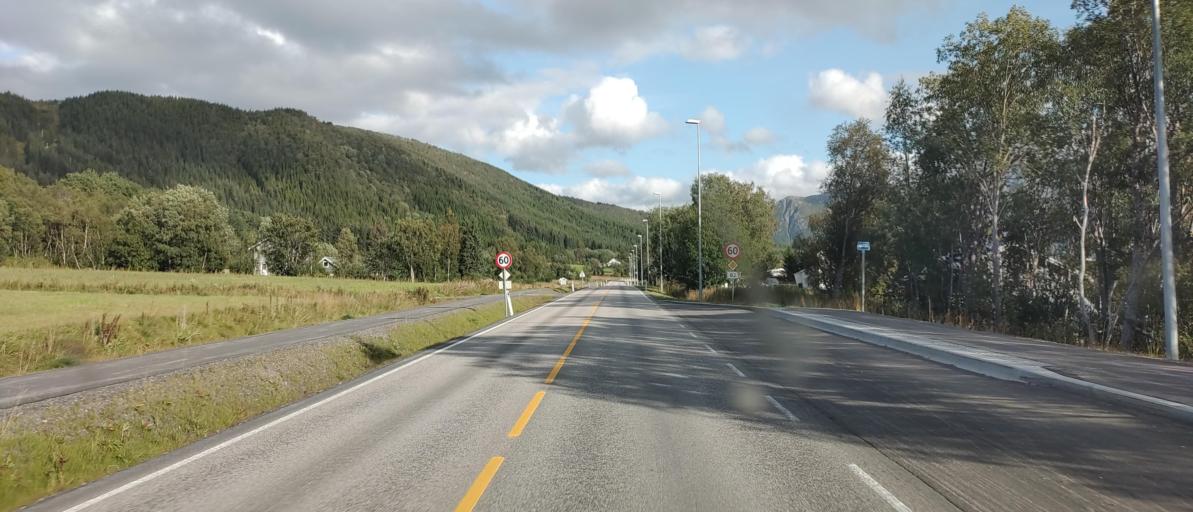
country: NO
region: Nordland
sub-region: Sortland
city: Sortland
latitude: 68.7515
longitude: 15.4802
